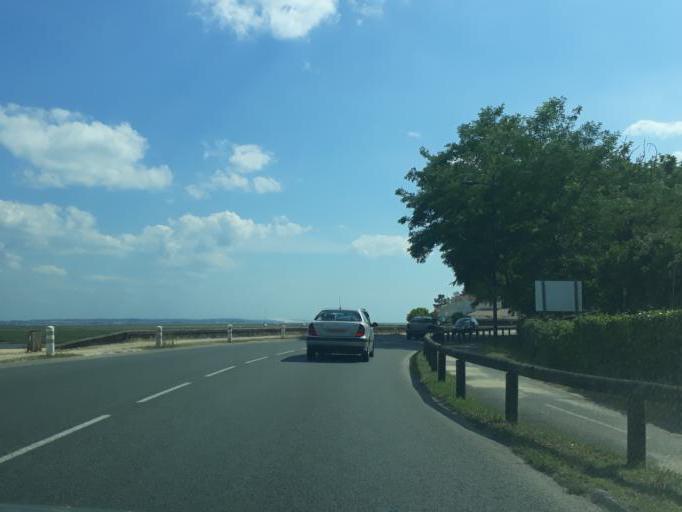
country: FR
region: Aquitaine
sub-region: Departement de la Gironde
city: Ares
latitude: 44.7443
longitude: -1.1814
